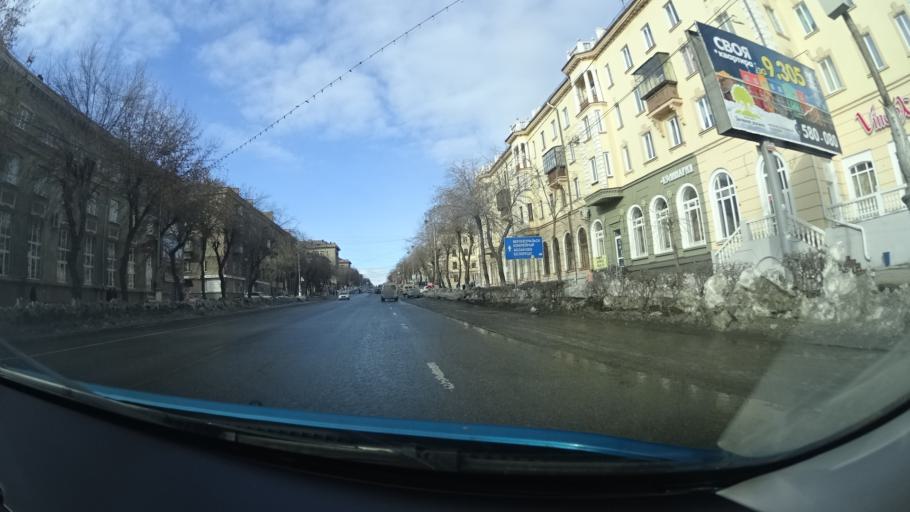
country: RU
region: Chelyabinsk
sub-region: Gorod Magnitogorsk
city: Magnitogorsk
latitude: 53.4246
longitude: 58.9837
